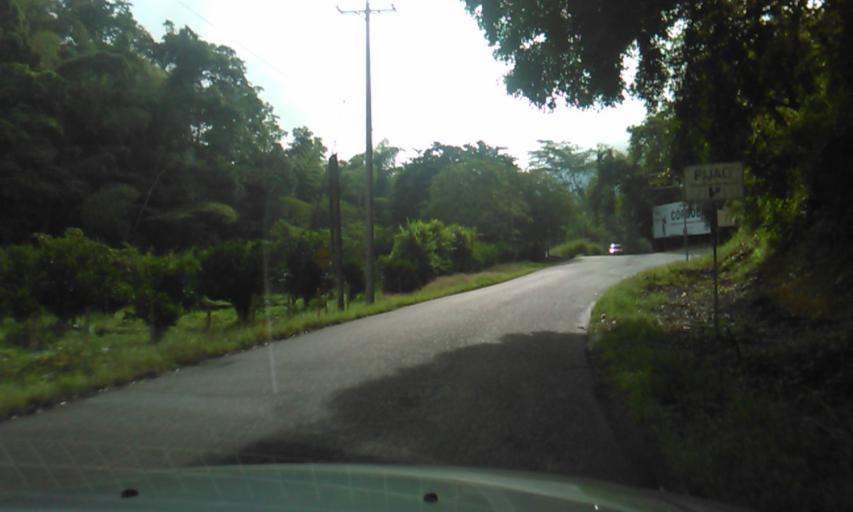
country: CO
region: Quindio
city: Cordoba
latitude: 4.4043
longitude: -75.7260
